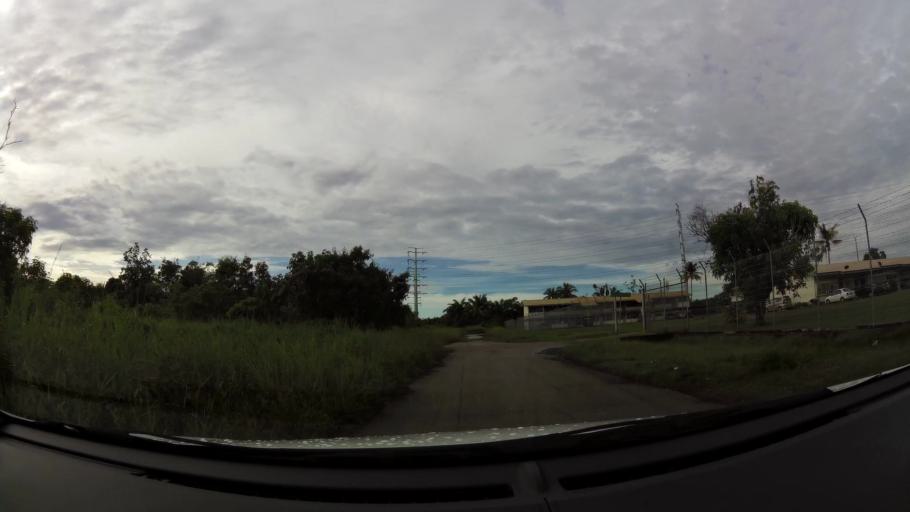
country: BN
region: Belait
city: Seria
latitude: 4.6163
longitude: 114.3462
